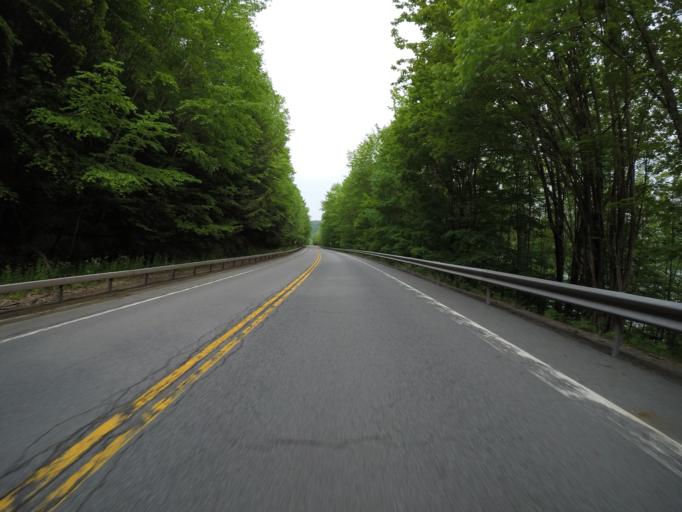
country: US
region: New York
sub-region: Sullivan County
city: Livingston Manor
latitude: 42.0891
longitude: -74.8278
